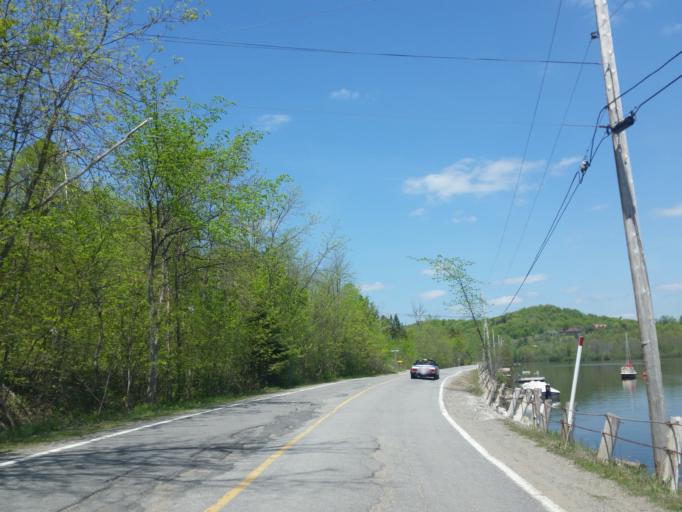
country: CA
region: Quebec
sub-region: Outaouais
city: Wakefield
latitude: 45.5972
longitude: -75.8820
